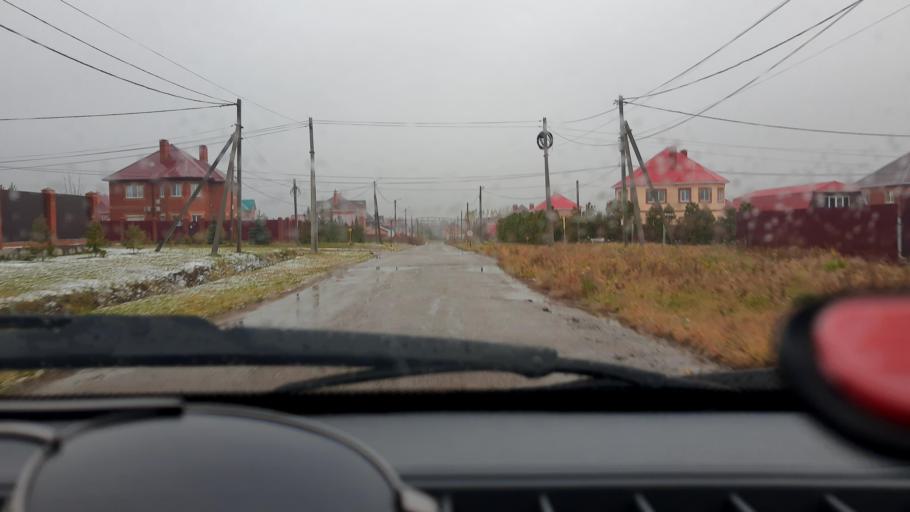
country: RU
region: Bashkortostan
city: Kabakovo
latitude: 54.6220
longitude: 56.1301
